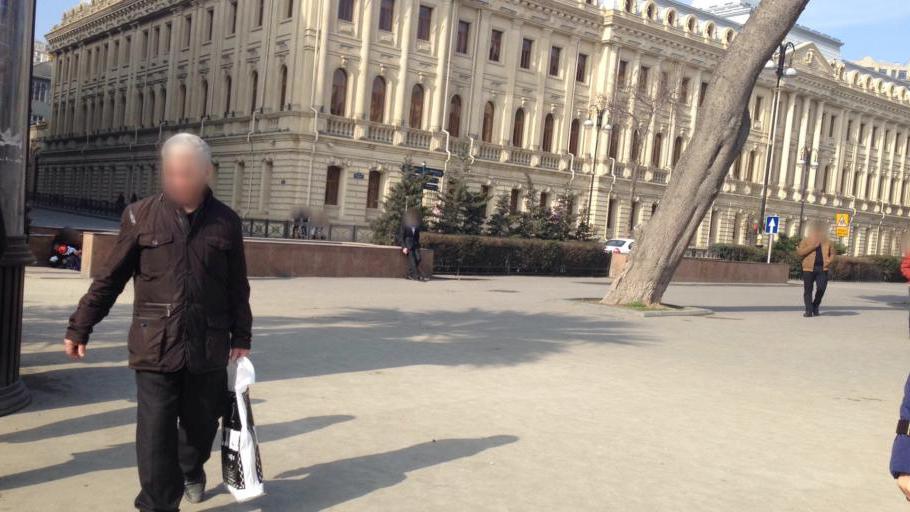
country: AZ
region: Baki
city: Badamdar
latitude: 40.3658
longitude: 49.8313
